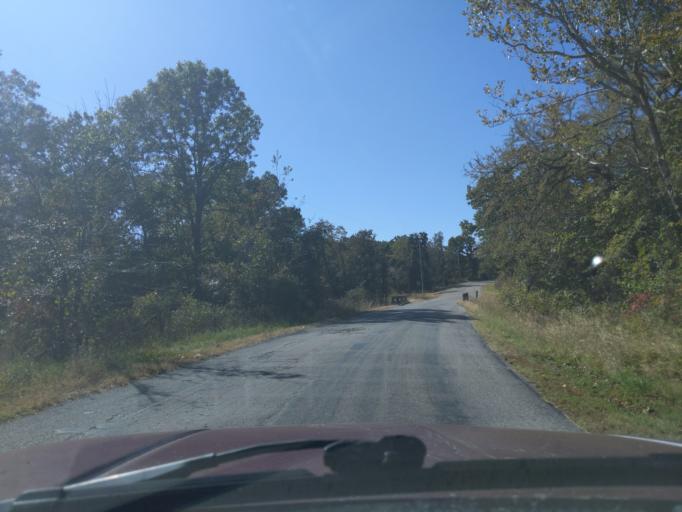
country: US
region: Oklahoma
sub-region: Creek County
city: Bristow
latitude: 35.7059
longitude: -96.4052
